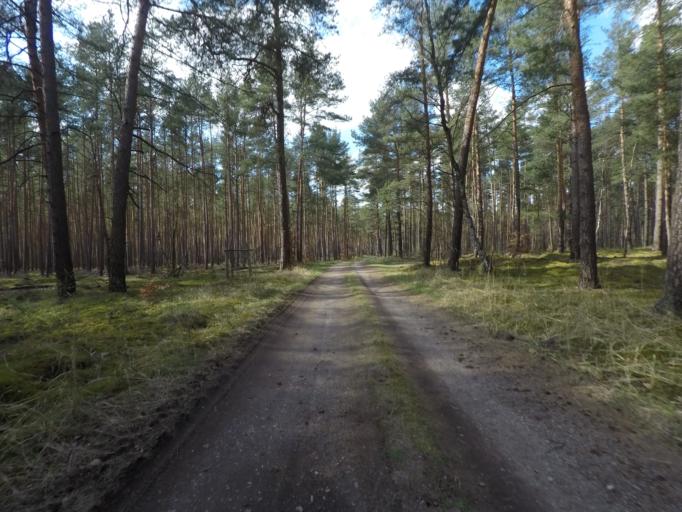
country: DE
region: Brandenburg
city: Melchow
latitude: 52.8190
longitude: 13.6905
